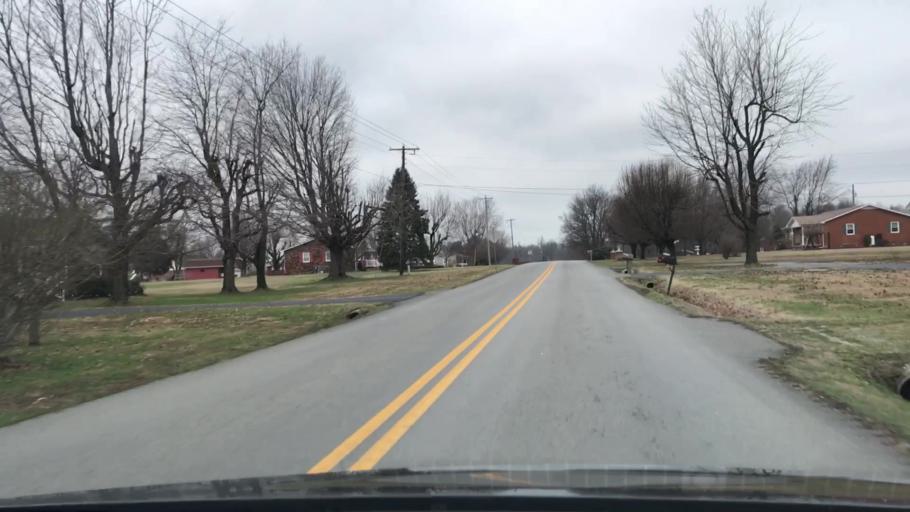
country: US
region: Kentucky
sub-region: Muhlenberg County
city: Morehead
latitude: 37.3571
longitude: -87.2300
